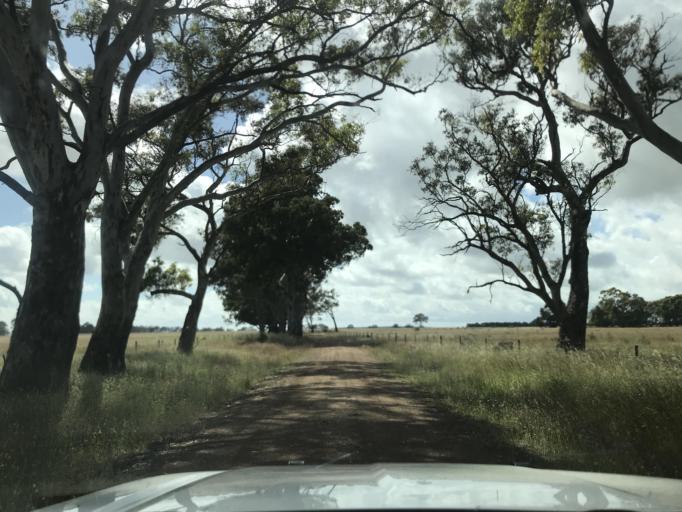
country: AU
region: South Australia
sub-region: Wattle Range
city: Penola
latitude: -37.2177
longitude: 141.3371
